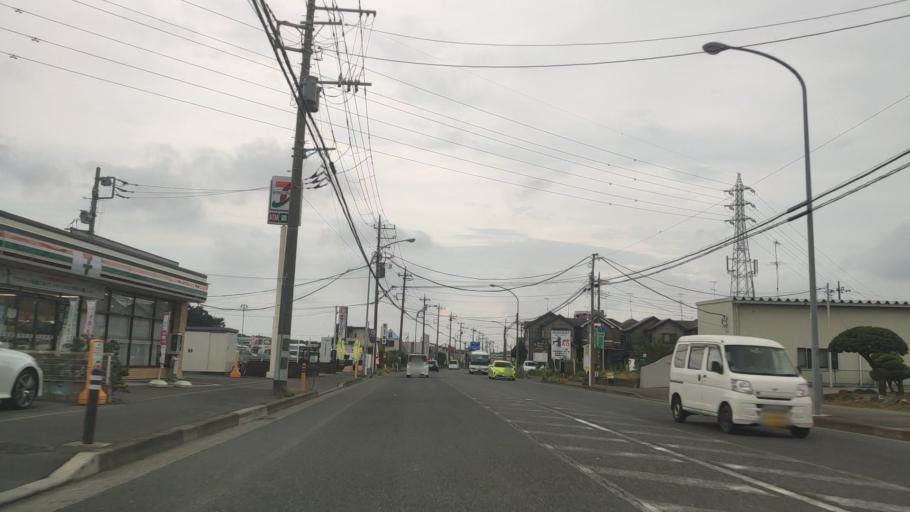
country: JP
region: Kanagawa
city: Minami-rinkan
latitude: 35.4293
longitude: 139.4845
